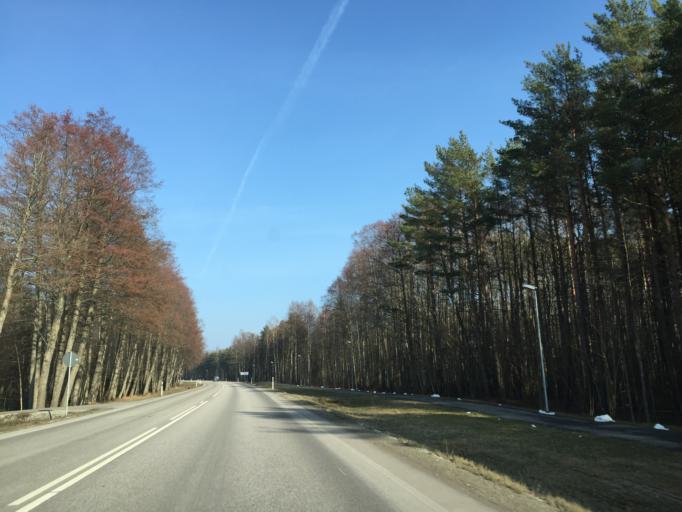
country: EE
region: Saare
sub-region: Kuressaare linn
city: Kuressaare
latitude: 58.2213
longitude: 22.3531
